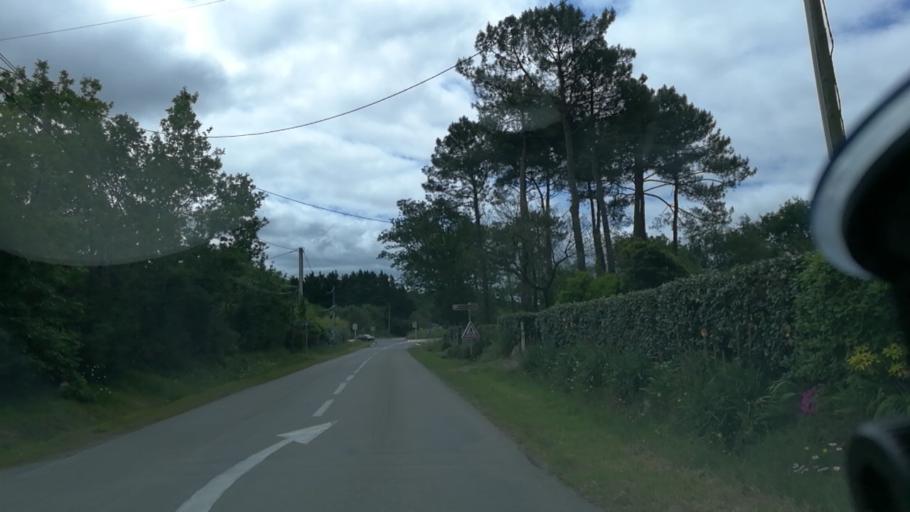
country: FR
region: Brittany
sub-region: Departement du Morbihan
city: Penestin
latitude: 47.4801
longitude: -2.4353
